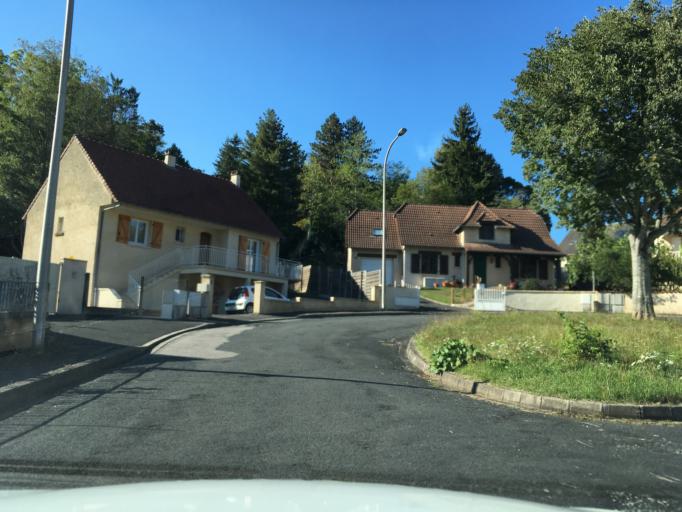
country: FR
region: Limousin
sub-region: Departement de la Correze
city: Malemort-sur-Correze
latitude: 45.1746
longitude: 1.5506
